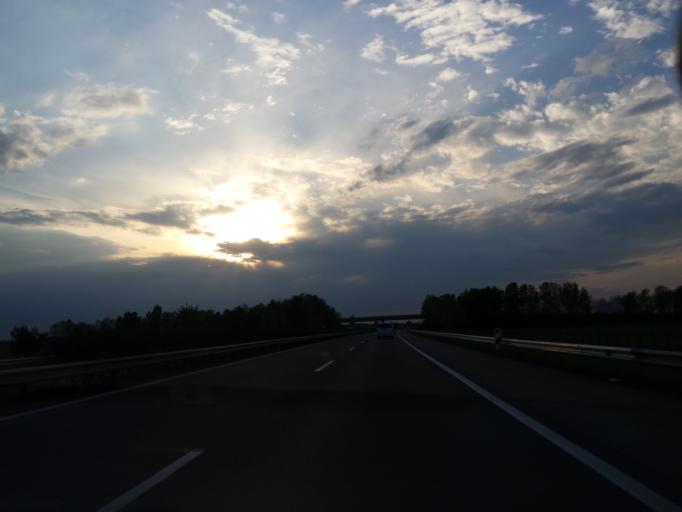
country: HU
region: Gyor-Moson-Sopron
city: Abda
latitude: 47.6918
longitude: 17.5200
